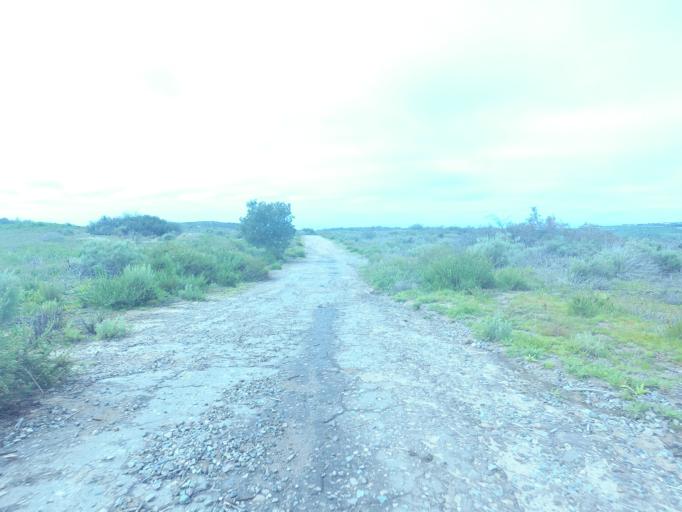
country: US
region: California
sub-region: Orange County
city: Laguna Beach
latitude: 33.5733
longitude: -117.7954
